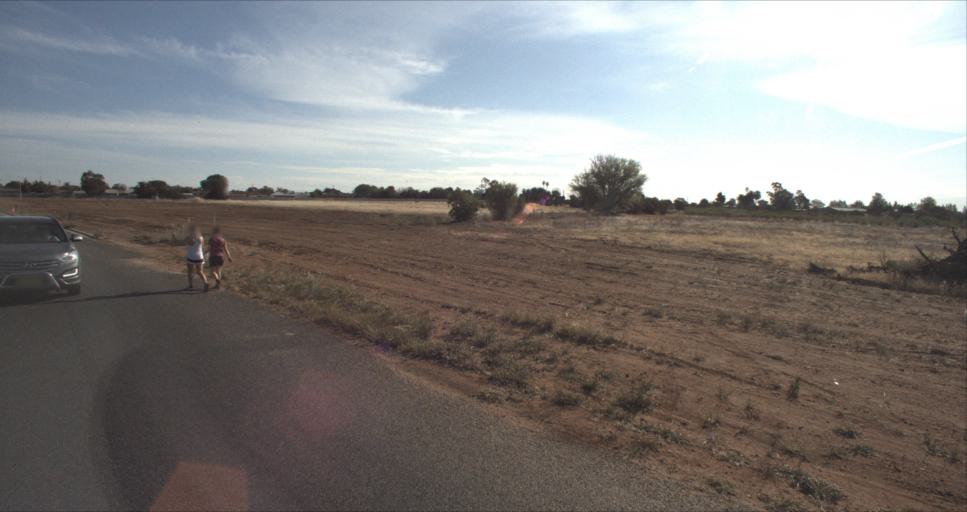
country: AU
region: New South Wales
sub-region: Leeton
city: Leeton
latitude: -34.5421
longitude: 146.4000
